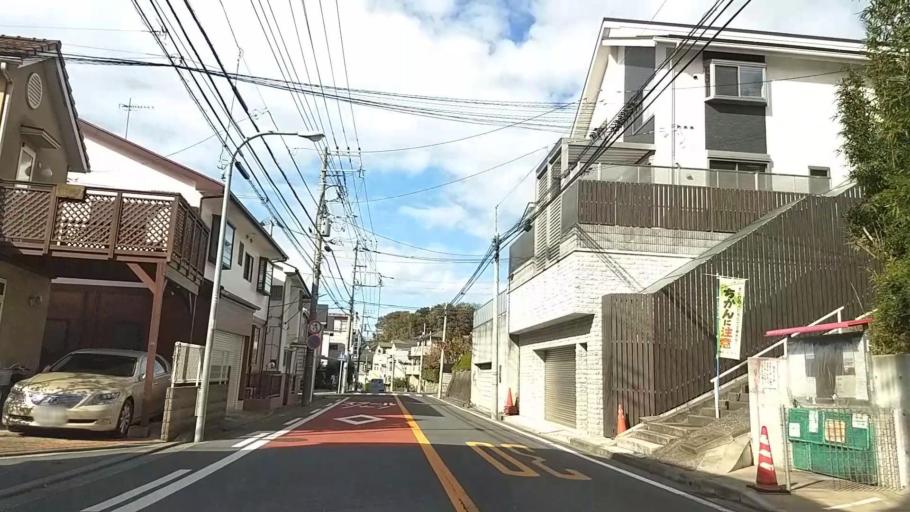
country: JP
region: Kanagawa
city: Yokohama
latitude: 35.5047
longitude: 139.6589
